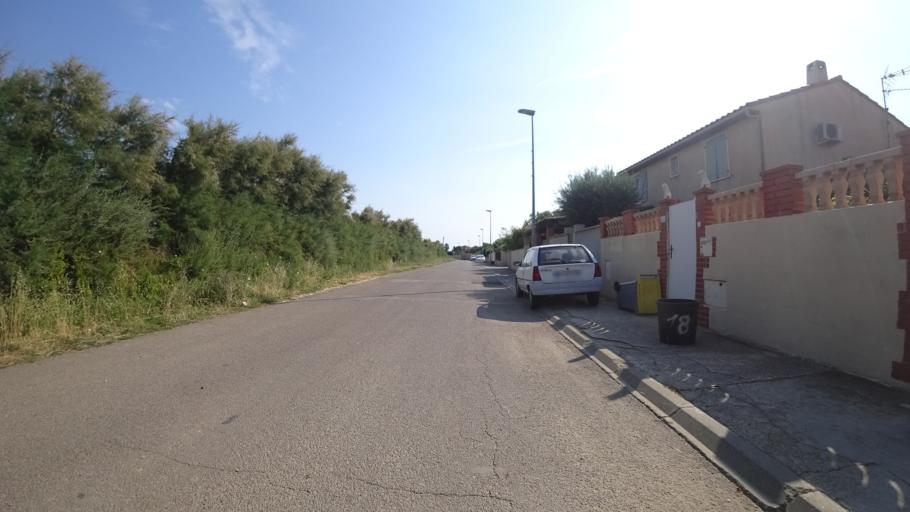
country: FR
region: Languedoc-Roussillon
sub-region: Departement des Pyrenees-Orientales
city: Saint-Laurent-de-la-Salanque
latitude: 42.7760
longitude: 3.0100
